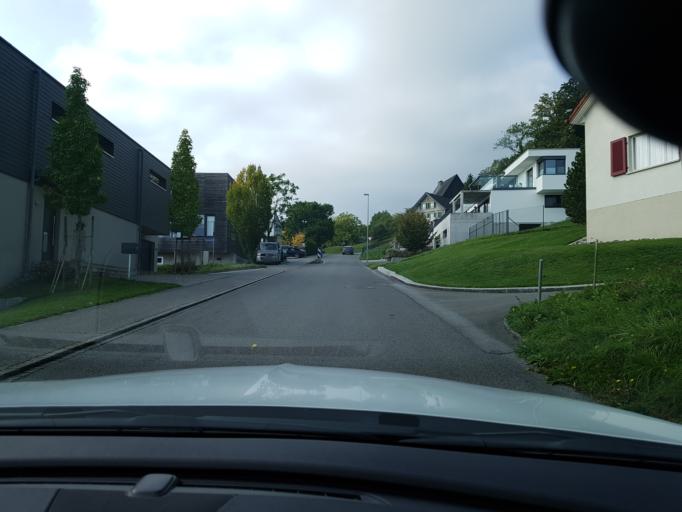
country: CH
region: Saint Gallen
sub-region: Wahlkreis Rheintal
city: Altstatten
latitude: 47.3882
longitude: 9.5498
